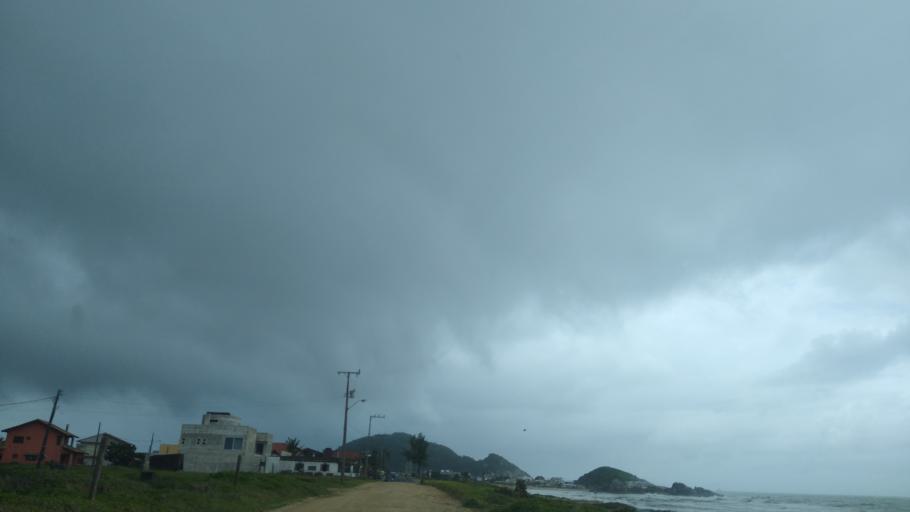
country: BR
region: Santa Catarina
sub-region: Sao Francisco Do Sul
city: Sao Francisco do Sul
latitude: -26.2408
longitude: -48.5071
